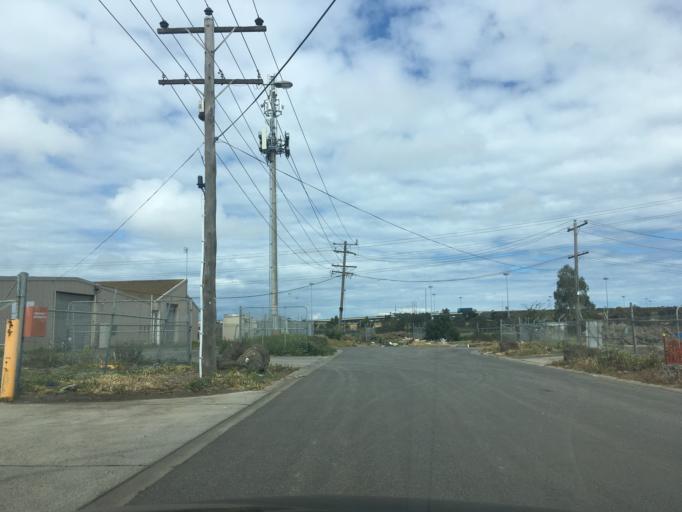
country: AU
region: Victoria
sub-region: Brimbank
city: Brooklyn
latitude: -37.8226
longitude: 144.8154
